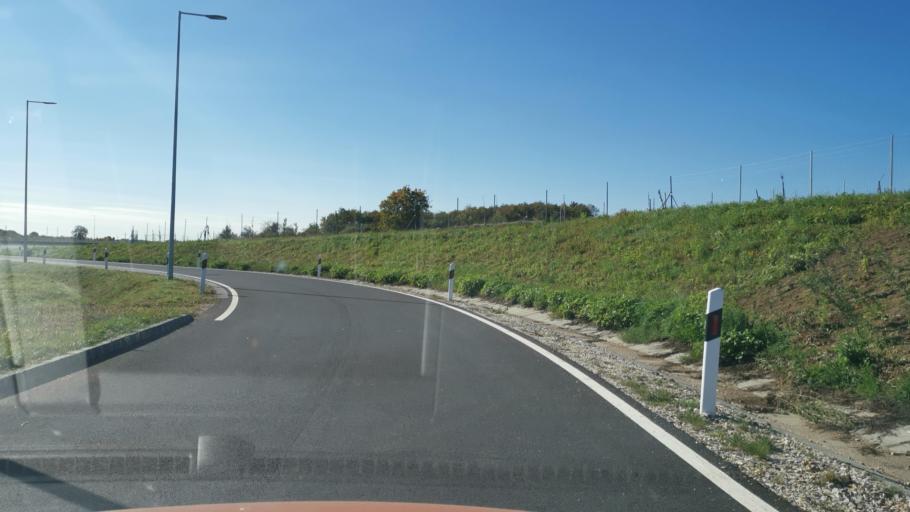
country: HU
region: Borsod-Abauj-Zemplen
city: Gonc
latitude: 48.5096
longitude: 21.2267
